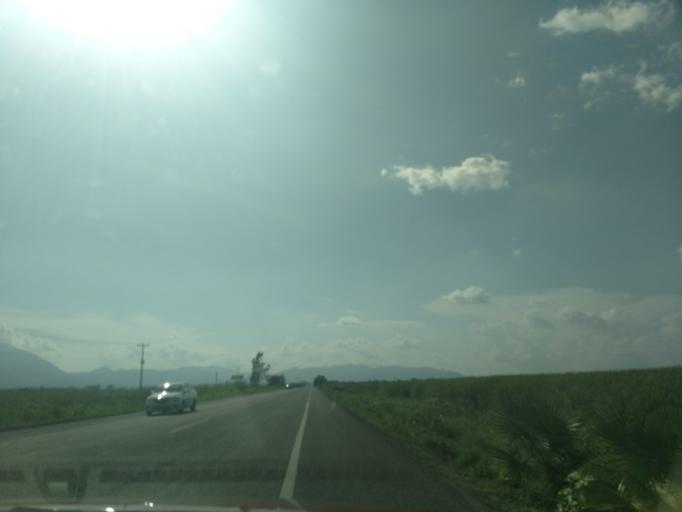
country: MX
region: Jalisco
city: Teuchitlan
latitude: 20.6824
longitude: -103.8585
